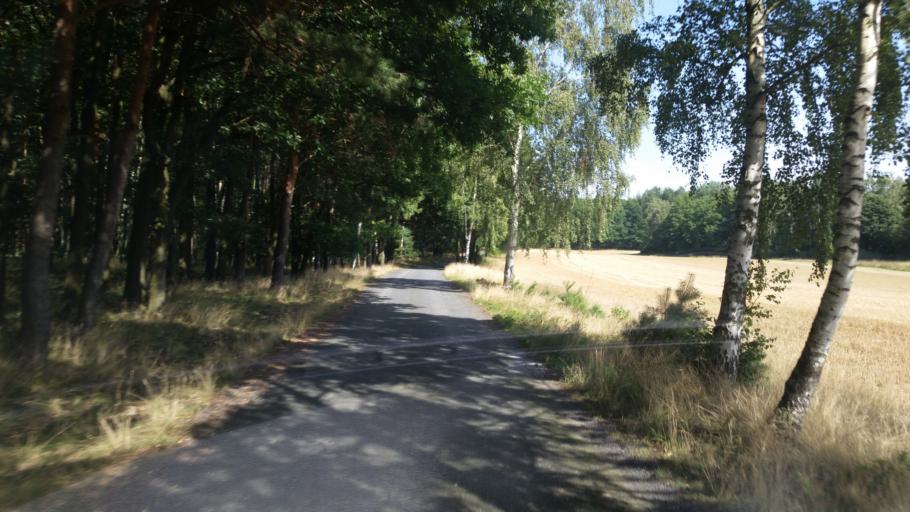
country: DE
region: Saxony
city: Wiednitz
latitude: 51.3283
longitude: 14.0281
